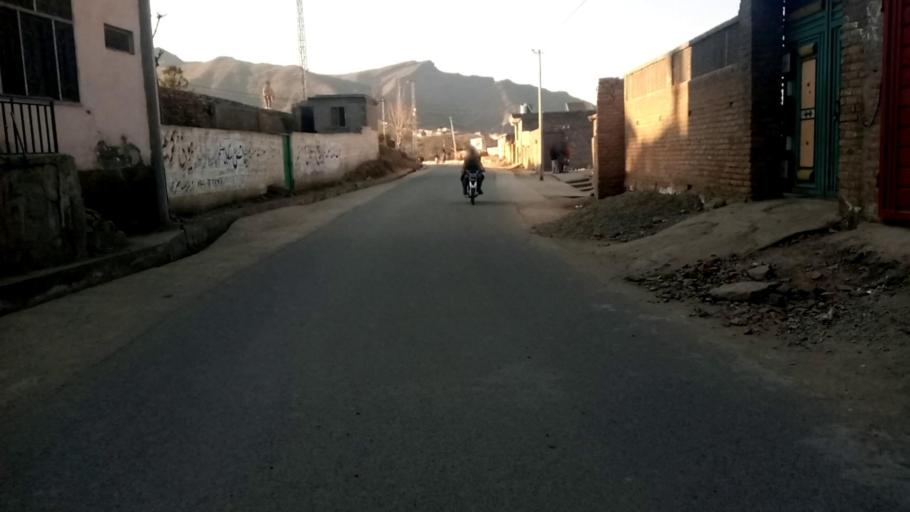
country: PK
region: Khyber Pakhtunkhwa
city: Saidu Sharif
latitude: 34.7430
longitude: 72.3573
